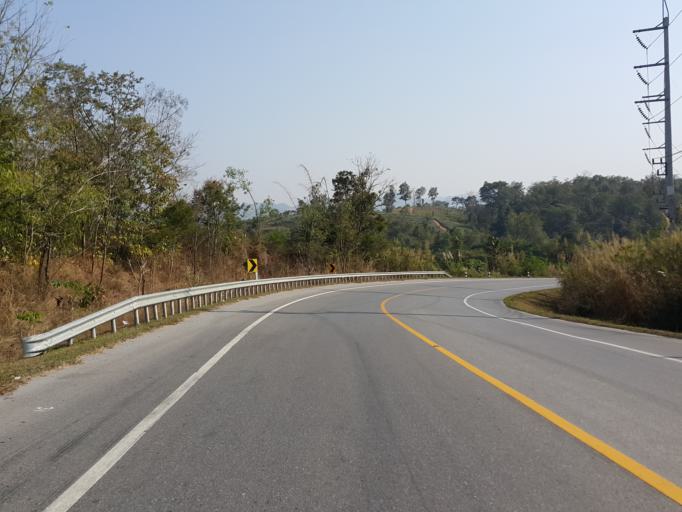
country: TH
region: Lampang
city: Chae Hom
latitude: 18.6067
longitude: 99.5474
